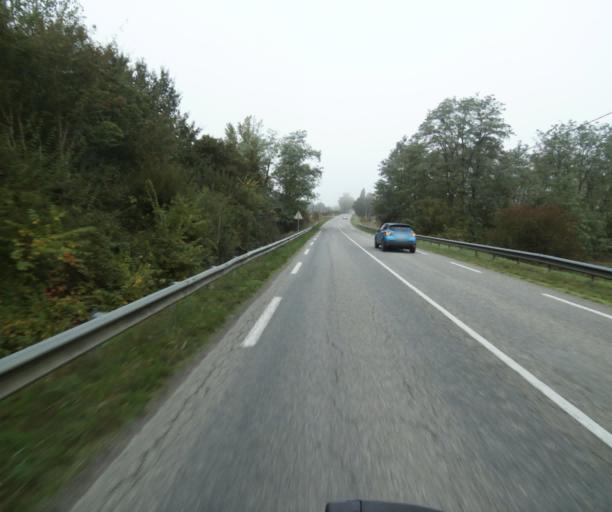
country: FR
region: Midi-Pyrenees
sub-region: Departement du Tarn-et-Garonne
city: Saint-Nauphary
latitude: 43.9487
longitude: 1.4522
